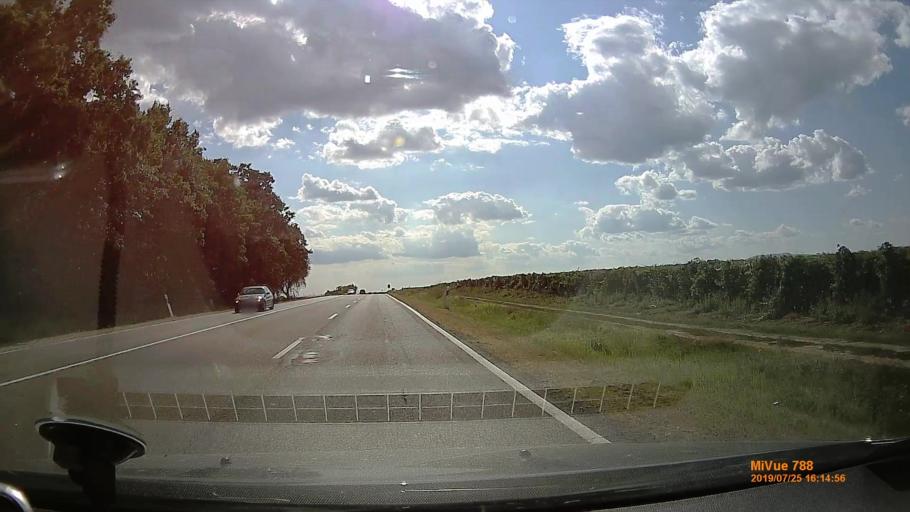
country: HU
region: Heves
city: Kerecsend
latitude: 47.7918
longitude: 20.3180
